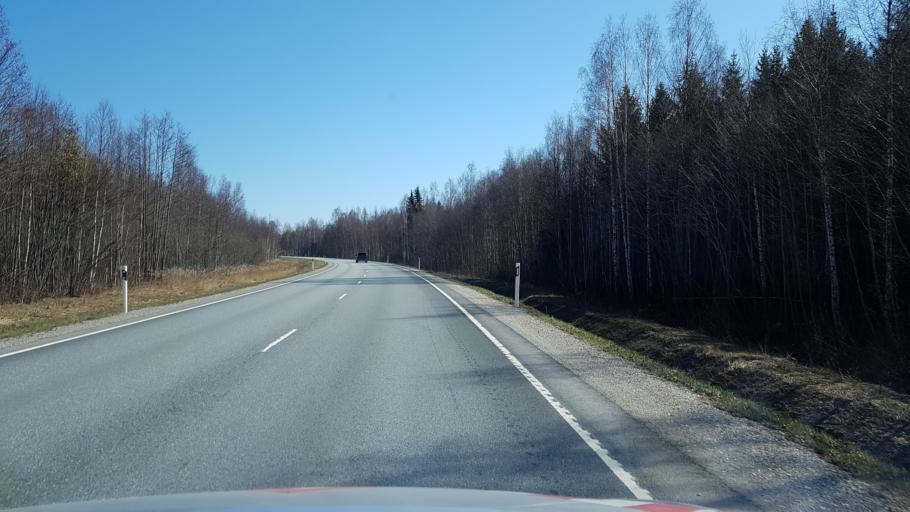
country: EE
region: Jogevamaa
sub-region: Mustvee linn
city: Mustvee
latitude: 58.8435
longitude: 26.9152
